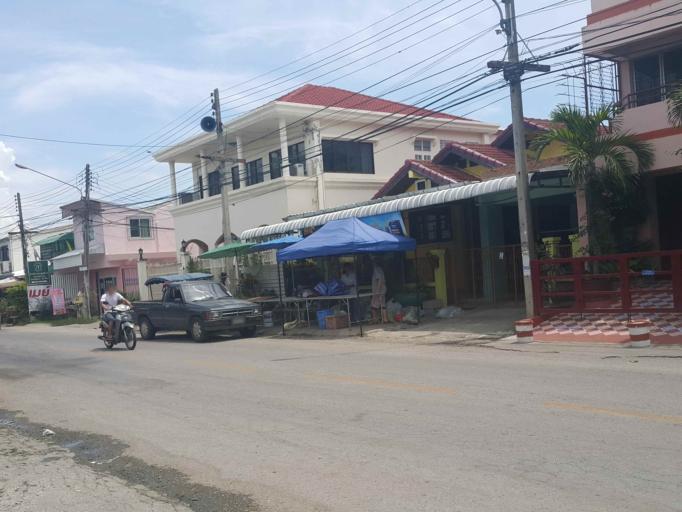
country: TH
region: Chiang Mai
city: Chiang Mai
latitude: 18.7636
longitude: 99.0111
